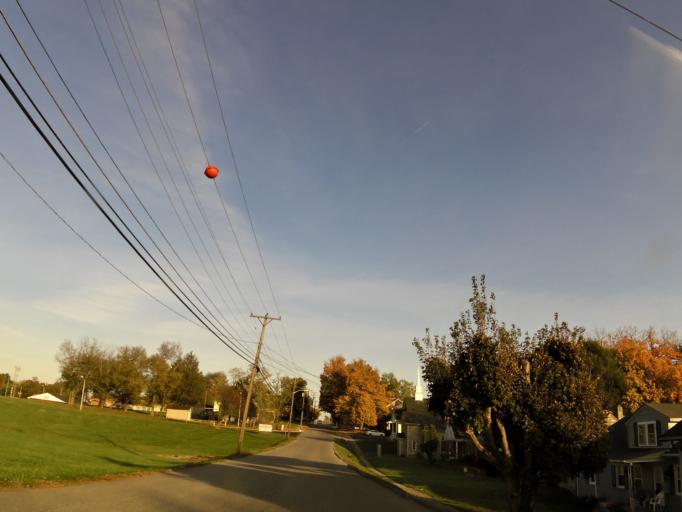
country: US
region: Kentucky
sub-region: Garrard County
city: Lancaster
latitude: 37.6212
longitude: -84.5844
